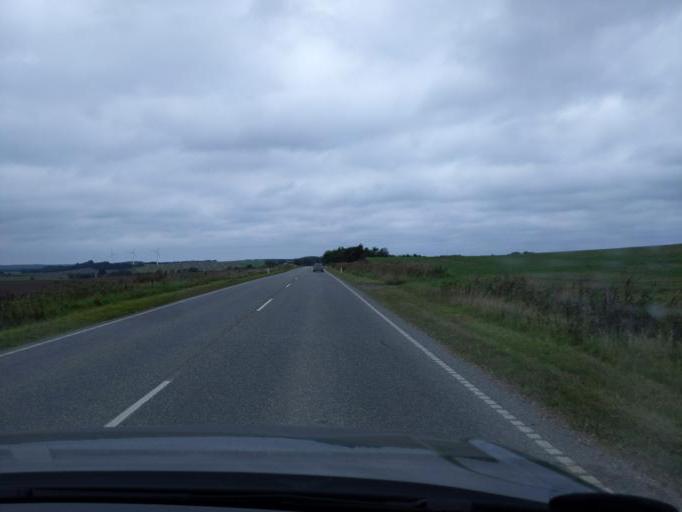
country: DK
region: North Denmark
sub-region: Mariagerfjord Kommune
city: Hobro
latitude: 56.5641
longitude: 9.8361
